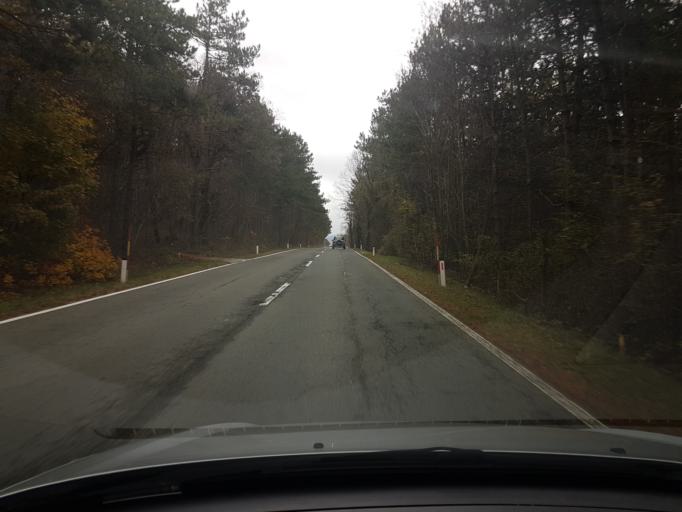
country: SI
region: Divaca
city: Divaca
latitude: 45.7293
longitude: 13.9666
